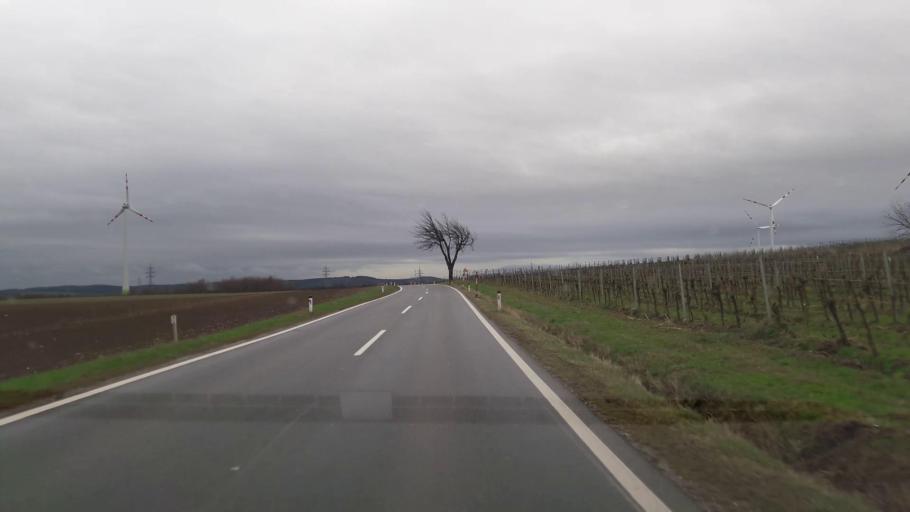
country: AT
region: Lower Austria
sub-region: Politischer Bezirk Bruck an der Leitha
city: Scharndorf
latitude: 48.0600
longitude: 16.7907
